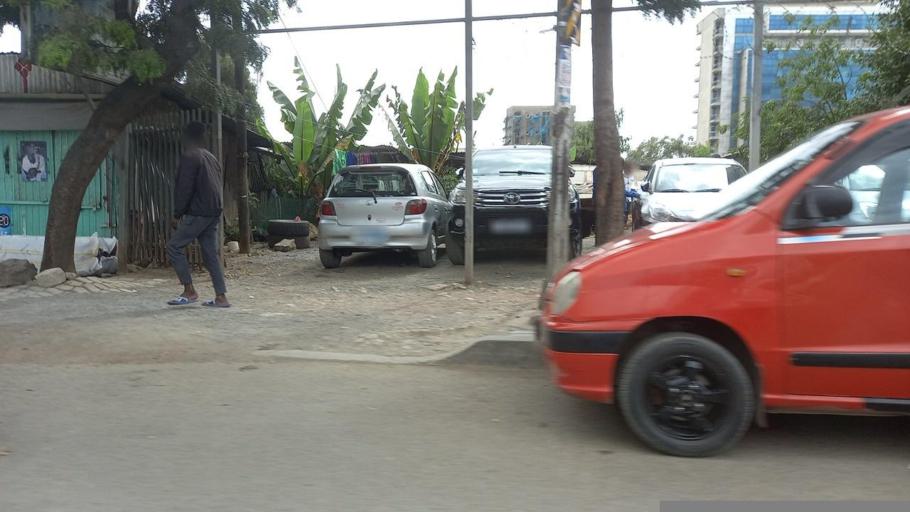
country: ET
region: Adis Abeba
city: Addis Ababa
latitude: 9.0208
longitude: 38.7960
